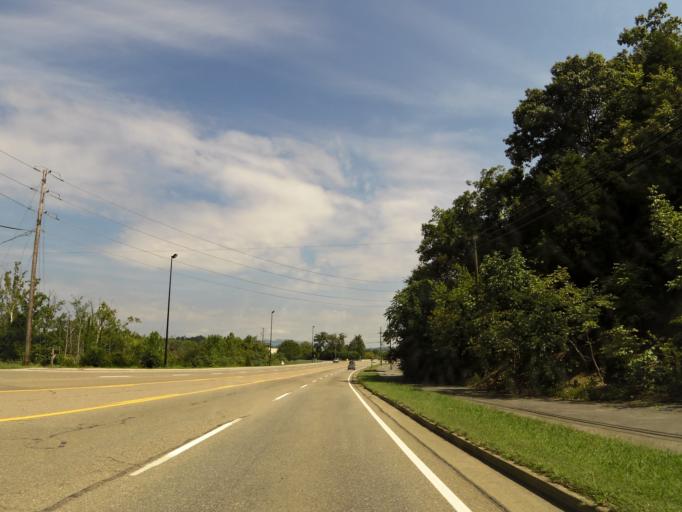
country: US
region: Tennessee
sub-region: Sullivan County
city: Kingsport
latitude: 36.5228
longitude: -82.5606
